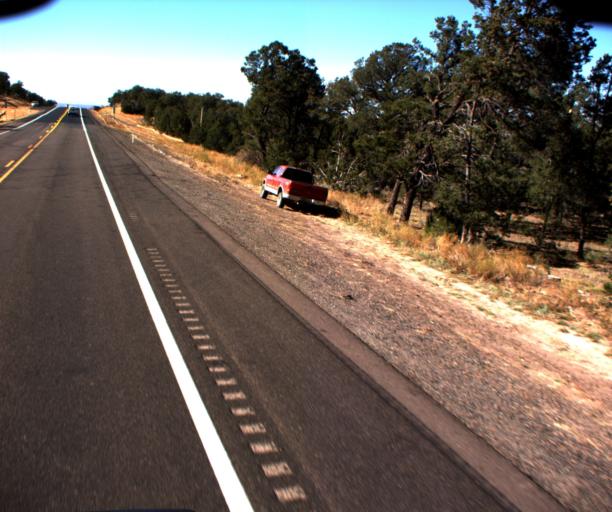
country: US
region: Arizona
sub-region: Apache County
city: Ganado
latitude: 35.7118
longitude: -109.3291
